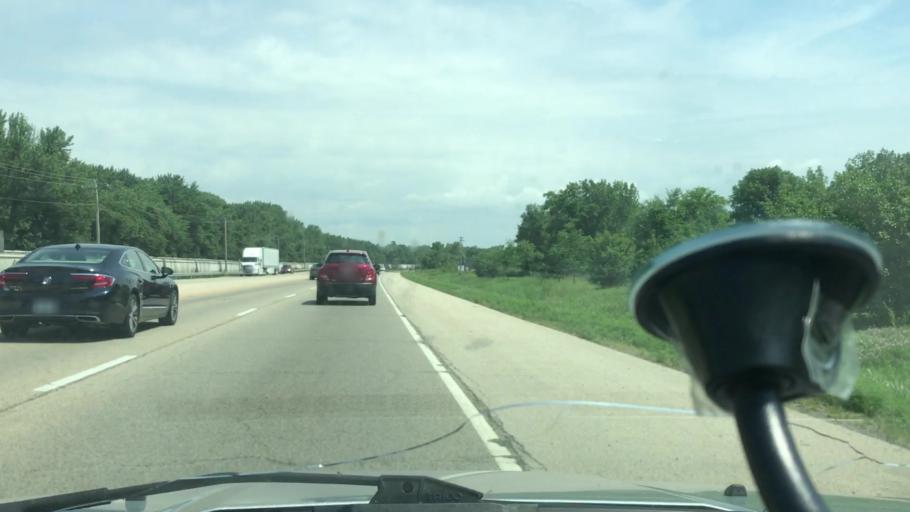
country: US
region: Illinois
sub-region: Tazewell County
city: North Pekin
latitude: 40.6065
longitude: -89.6358
